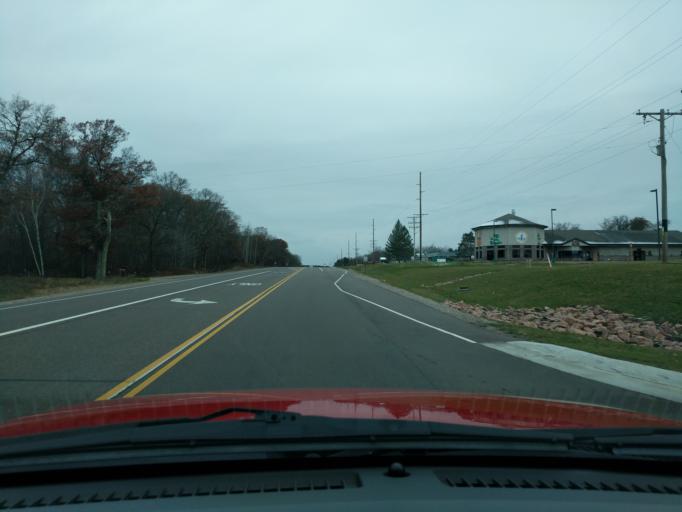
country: US
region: Wisconsin
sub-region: Burnett County
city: Siren
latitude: 45.8088
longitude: -92.2024
